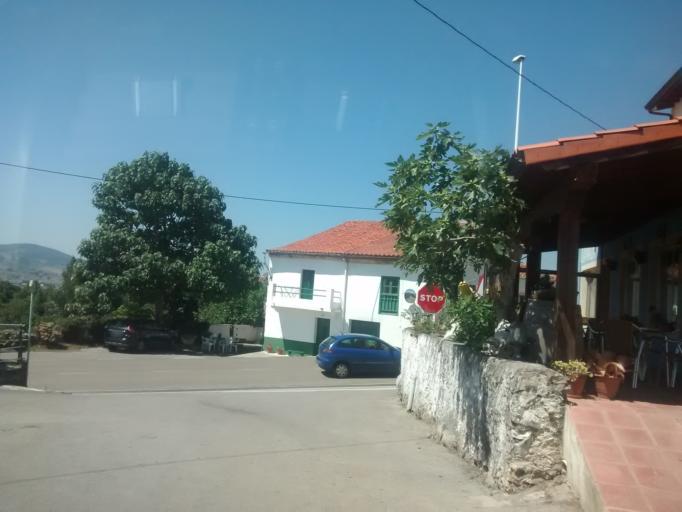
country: ES
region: Cantabria
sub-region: Provincia de Cantabria
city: Arnuero
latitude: 43.4770
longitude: -3.5684
